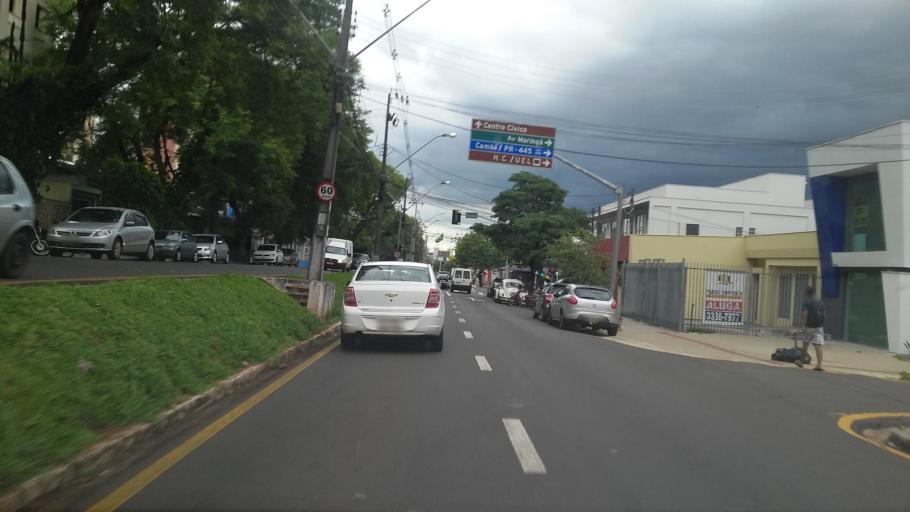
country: BR
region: Parana
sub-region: Londrina
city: Londrina
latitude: -23.3147
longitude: -51.1706
